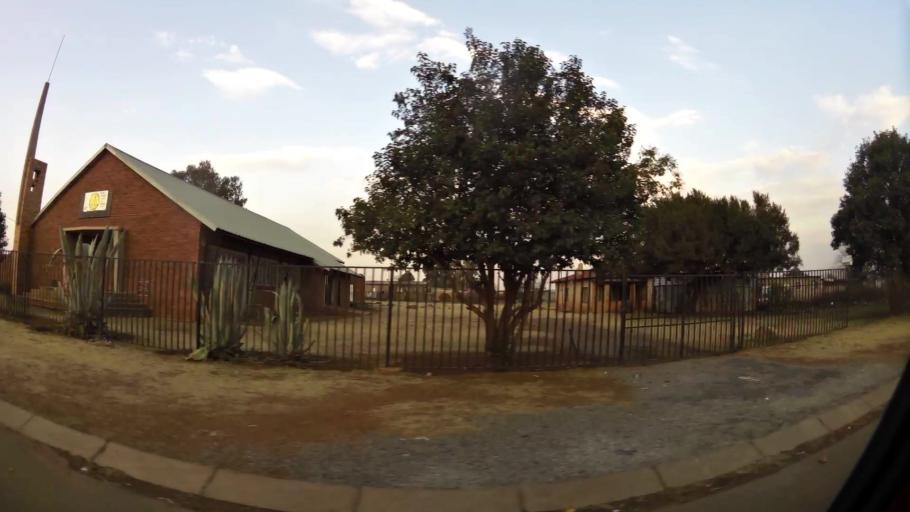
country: ZA
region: Gauteng
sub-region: City of Johannesburg Metropolitan Municipality
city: Orange Farm
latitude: -26.5386
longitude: 27.8498
